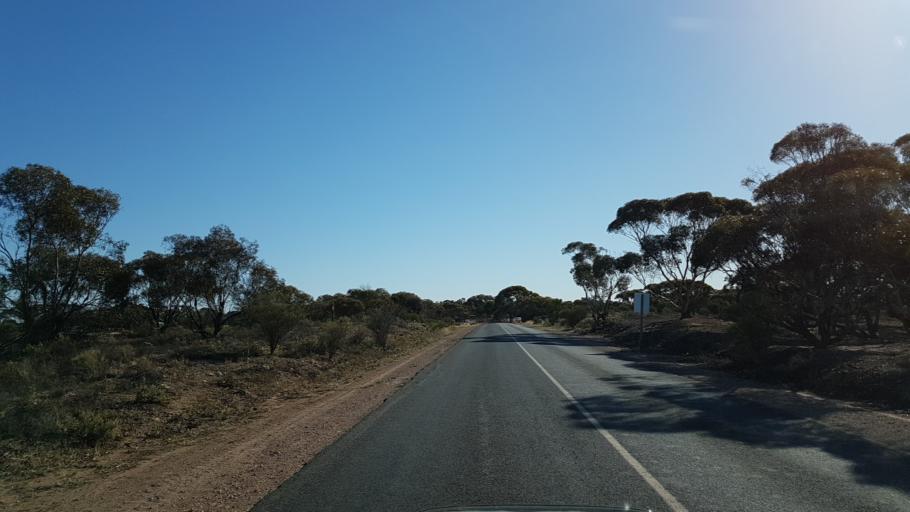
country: AU
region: South Australia
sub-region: Loxton Waikerie
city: Waikerie
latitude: -34.1860
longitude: 140.0197
